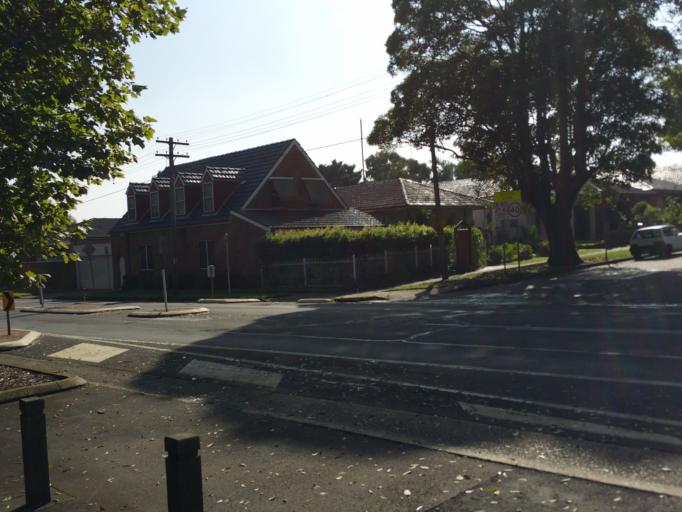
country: AU
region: New South Wales
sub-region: Canada Bay
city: Concord
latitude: -33.8631
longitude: 151.1049
